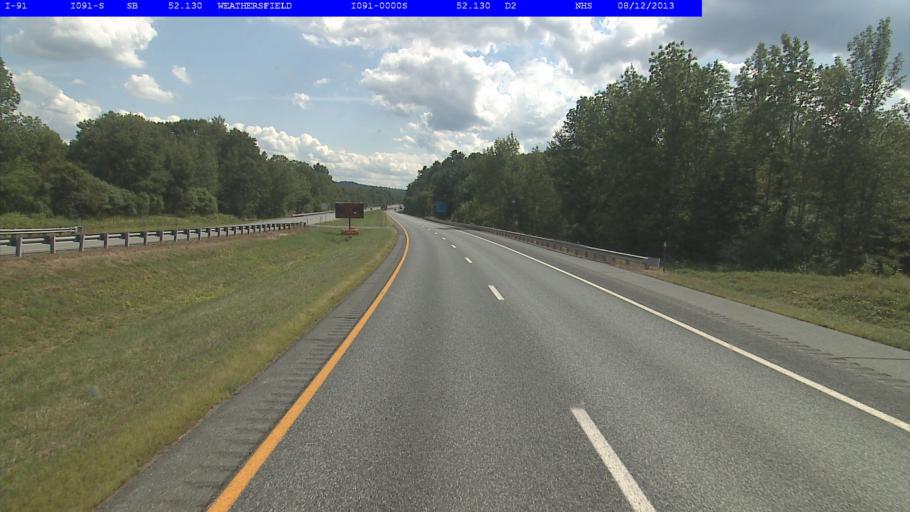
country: US
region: Vermont
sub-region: Windsor County
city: Windsor
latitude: 43.4136
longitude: -72.4156
